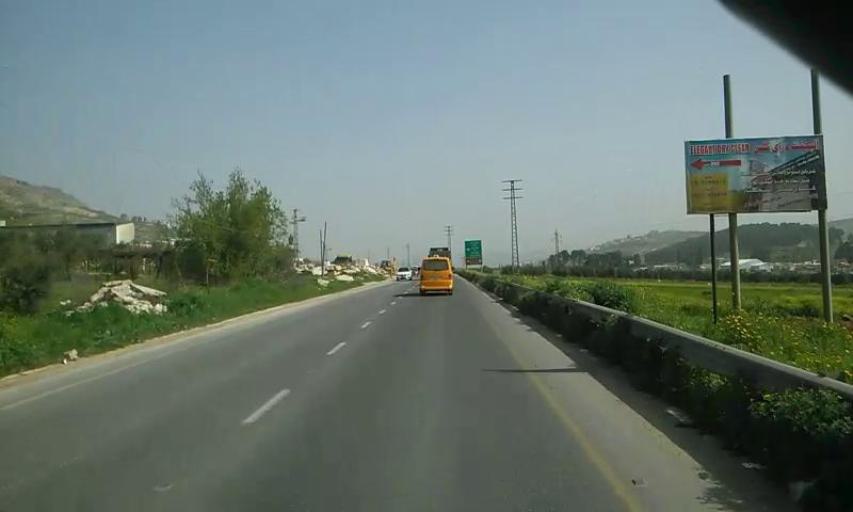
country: PS
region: West Bank
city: `Awarta
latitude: 32.1722
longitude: 35.2700
